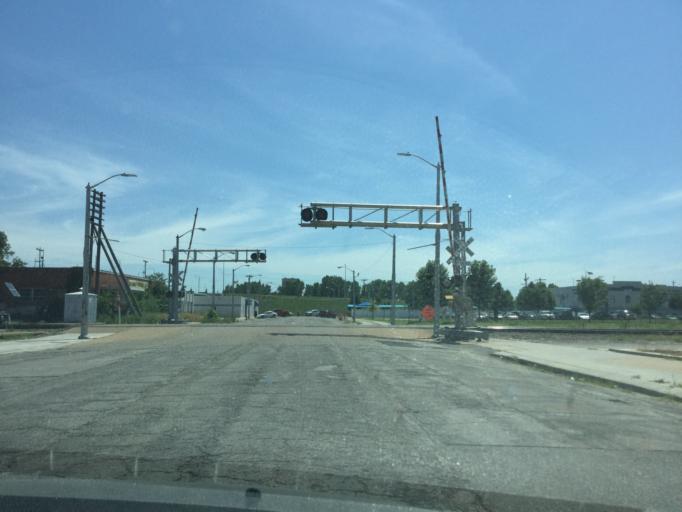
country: US
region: Kansas
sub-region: Shawnee County
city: Topeka
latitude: 39.0661
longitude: -95.6671
